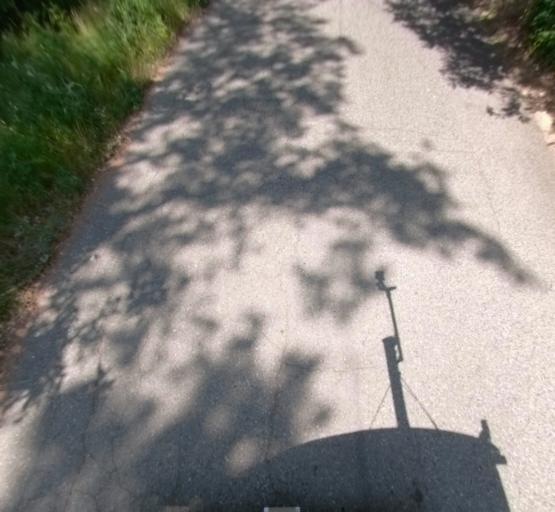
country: US
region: California
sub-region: Fresno County
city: Auberry
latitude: 37.2342
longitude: -119.4574
